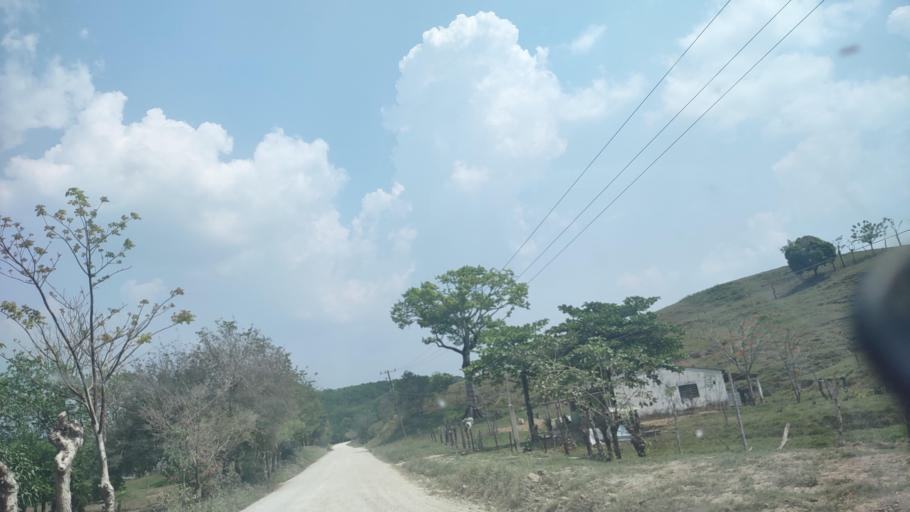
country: MX
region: Tabasco
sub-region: Huimanguillo
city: Francisco Rueda
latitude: 17.6077
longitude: -93.9081
